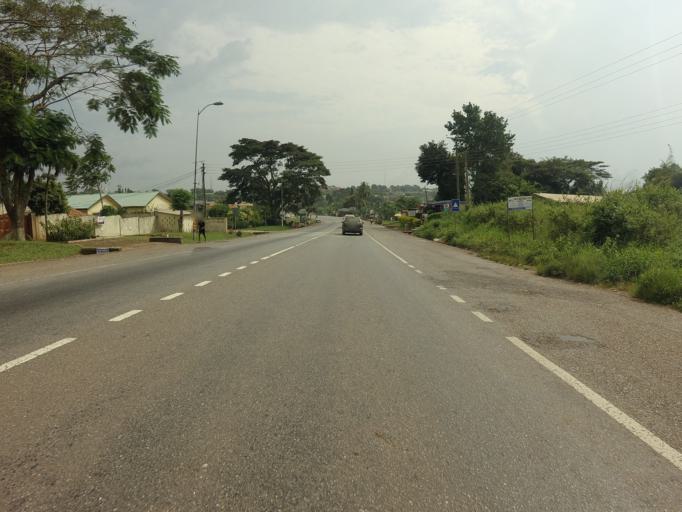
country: GH
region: Eastern
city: Aburi
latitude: 5.8112
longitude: -0.1849
